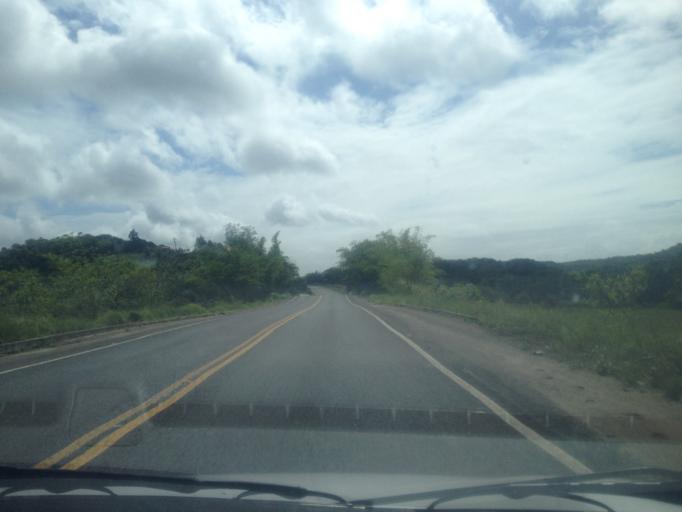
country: BR
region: Bahia
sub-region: Conde
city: Conde
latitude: -11.9579
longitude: -37.6702
